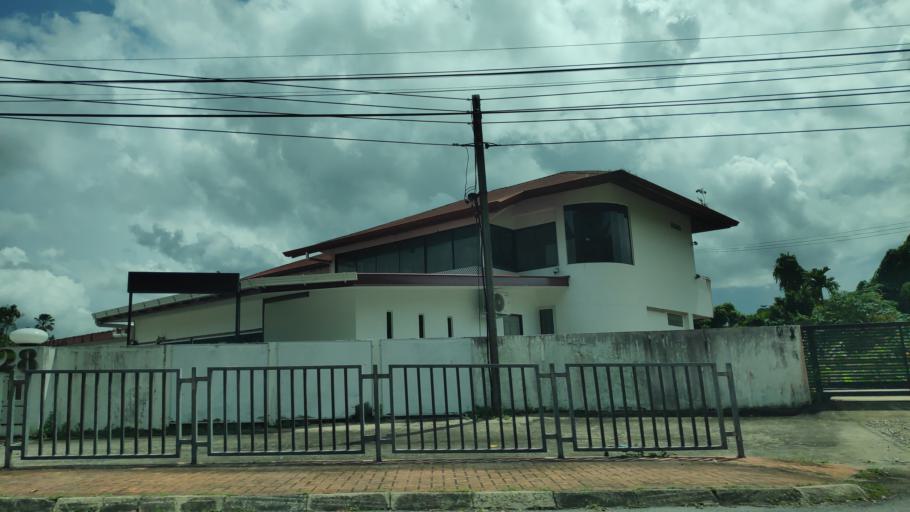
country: MY
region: Sarawak
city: Kuching
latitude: 1.5465
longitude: 110.3469
